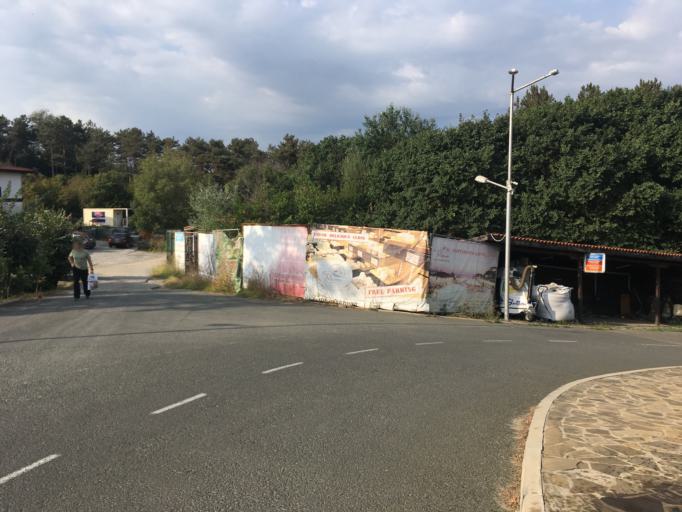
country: BG
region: Burgas
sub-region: Obshtina Sozopol
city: Sozopol
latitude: 42.4072
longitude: 27.6790
